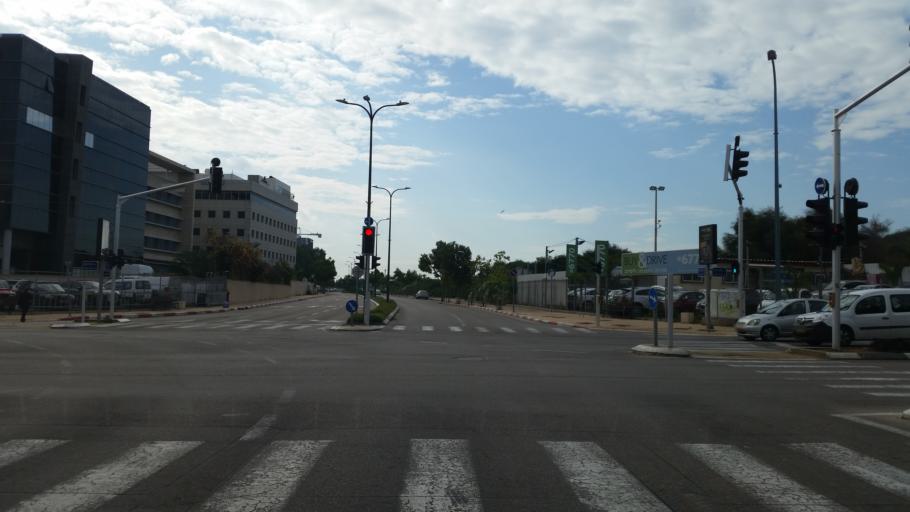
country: IL
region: Tel Aviv
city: Herzliya Pituah
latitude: 32.1632
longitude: 34.8062
